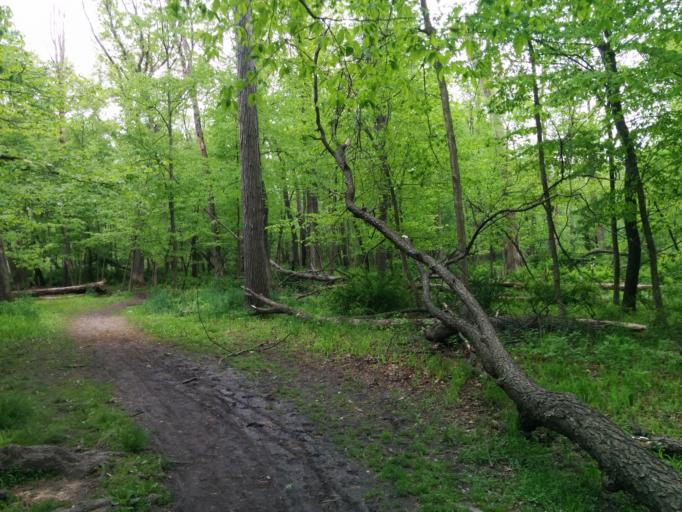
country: US
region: Illinois
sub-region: Cook County
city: Norridge
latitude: 41.9510
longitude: -87.8458
